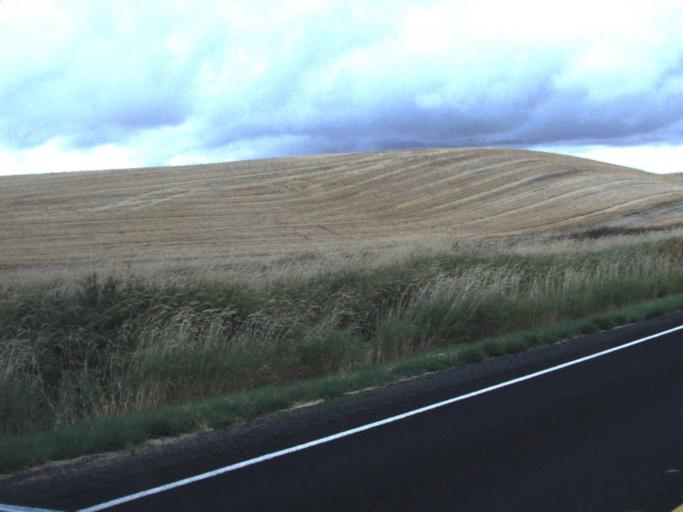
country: US
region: Washington
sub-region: Whitman County
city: Colfax
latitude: 47.1739
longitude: -117.2920
